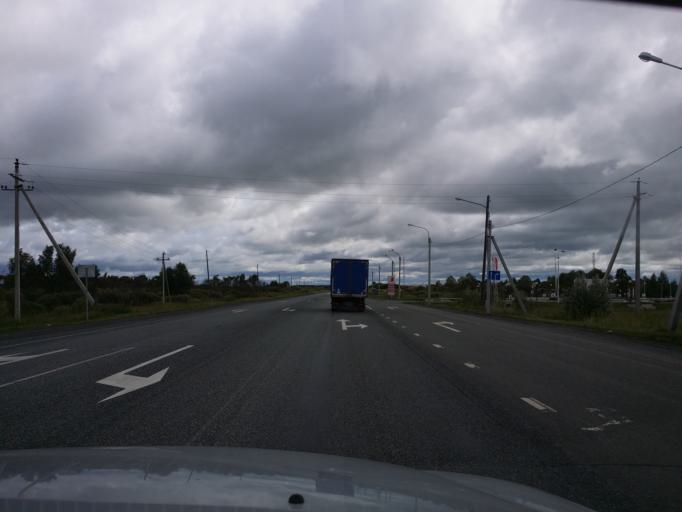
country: RU
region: Tjumen
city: Yarkovo
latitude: 57.2439
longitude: 66.7687
